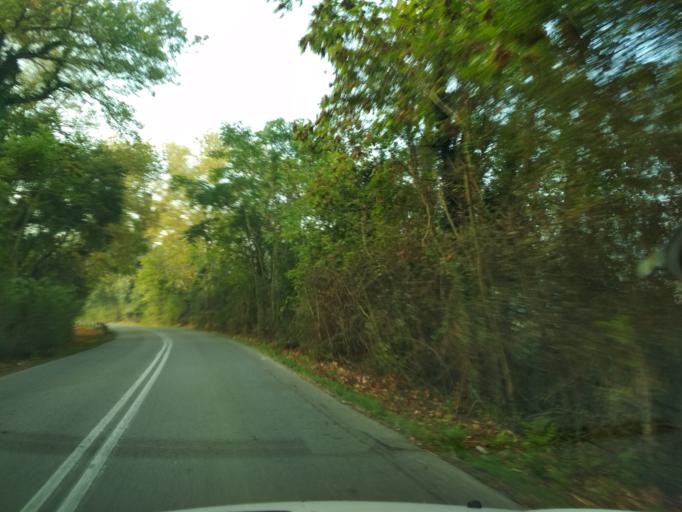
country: GR
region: Central Greece
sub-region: Nomos Evvoias
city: Prokopion
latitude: 38.7438
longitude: 23.4892
